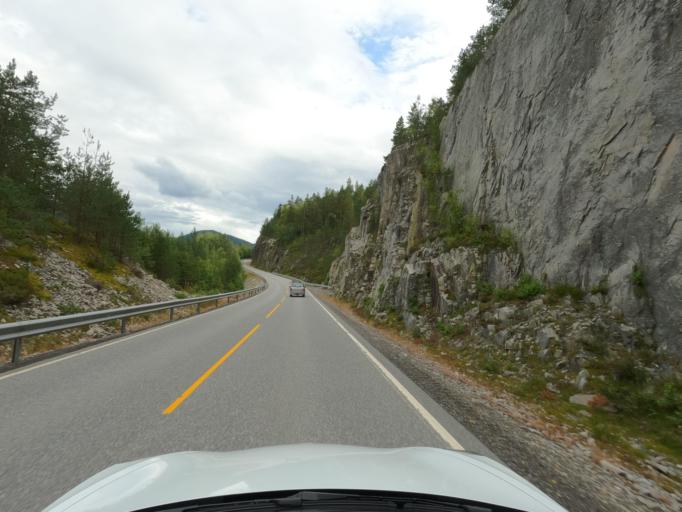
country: NO
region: Telemark
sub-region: Hjartdal
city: Sauland
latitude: 59.7853
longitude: 9.0051
